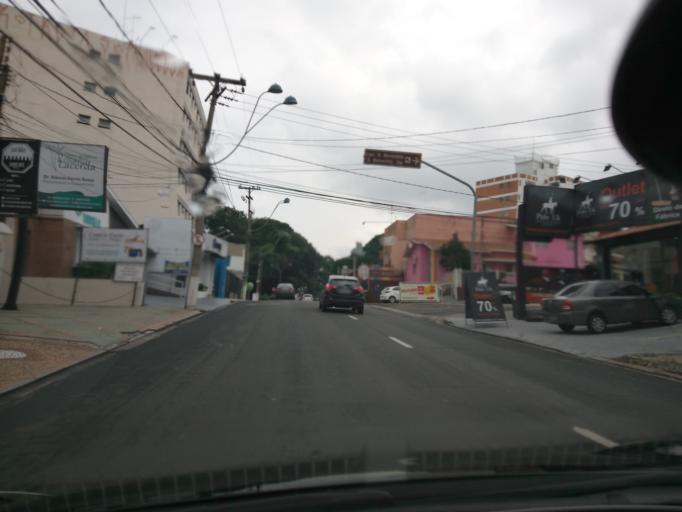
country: BR
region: Sao Paulo
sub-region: Campinas
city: Campinas
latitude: -22.9067
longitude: -47.0505
